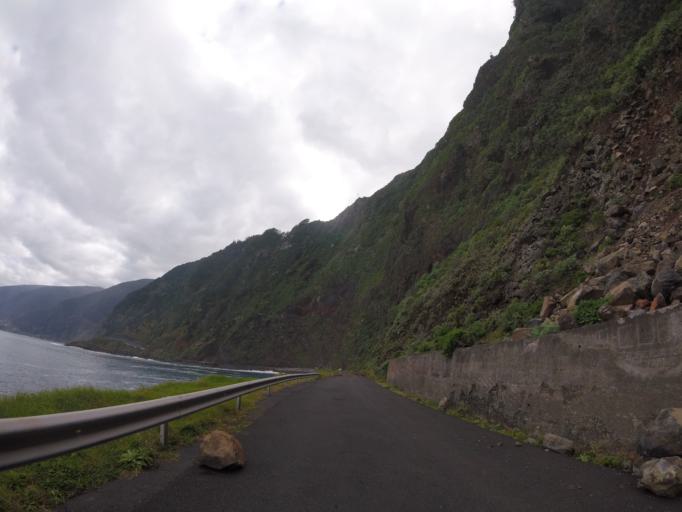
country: PT
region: Madeira
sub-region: Porto Moniz
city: Porto Moniz
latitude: 32.8514
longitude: -17.1500
